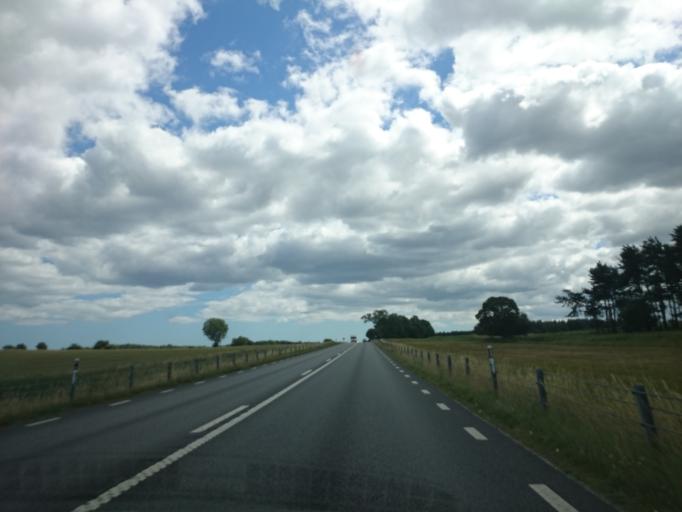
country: SE
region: Skane
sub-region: Kristianstads Kommun
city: Degeberga
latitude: 55.8216
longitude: 14.1176
